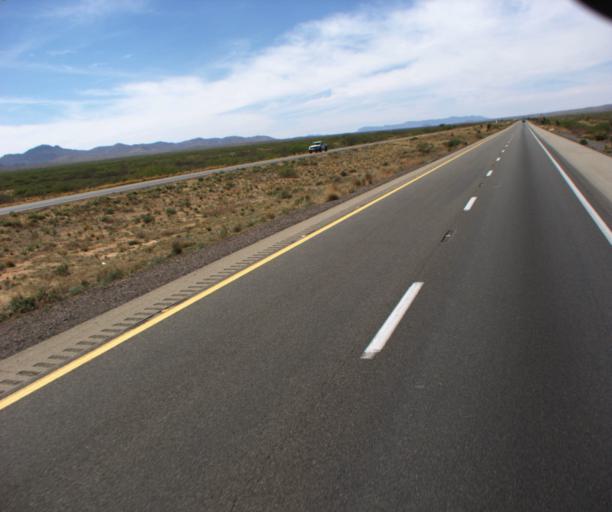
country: US
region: Arizona
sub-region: Cochise County
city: Willcox
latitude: 32.3402
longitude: -109.5604
